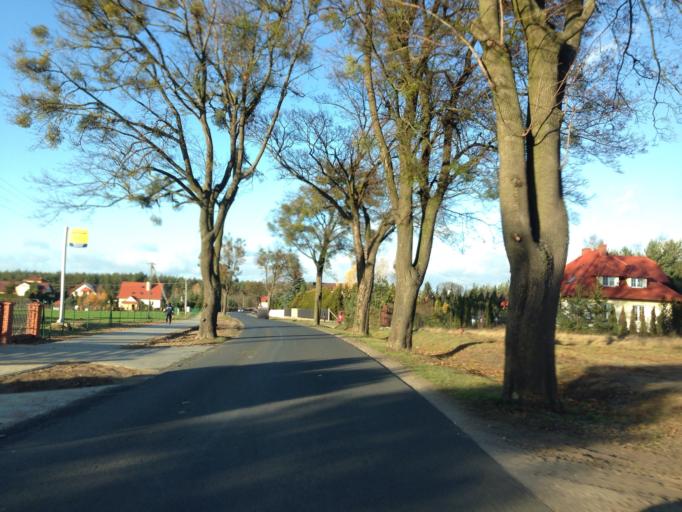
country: PL
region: Kujawsko-Pomorskie
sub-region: Powiat brodnicki
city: Brodnica
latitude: 53.2810
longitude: 19.3868
